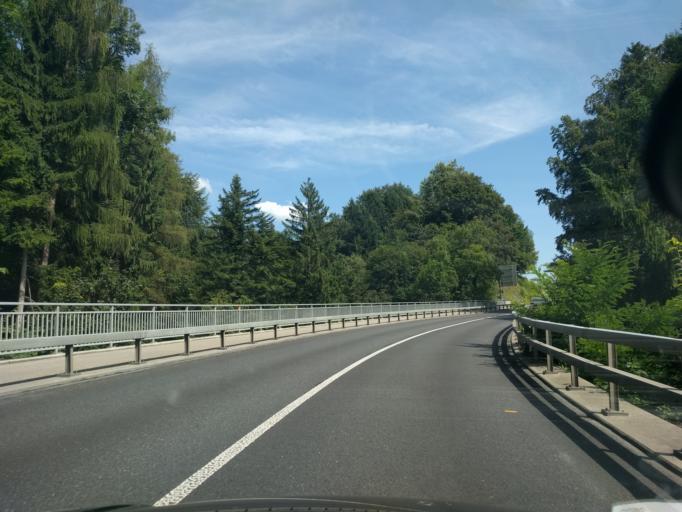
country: CH
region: Saint Gallen
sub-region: Wahlkreis See-Gaster
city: Schmerikon
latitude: 47.2439
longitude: 8.9505
